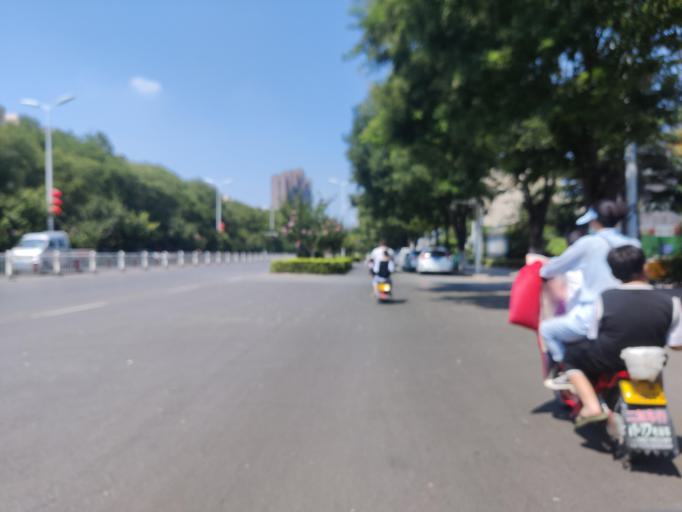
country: CN
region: Henan Sheng
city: Puyang
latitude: 35.7728
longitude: 115.0191
